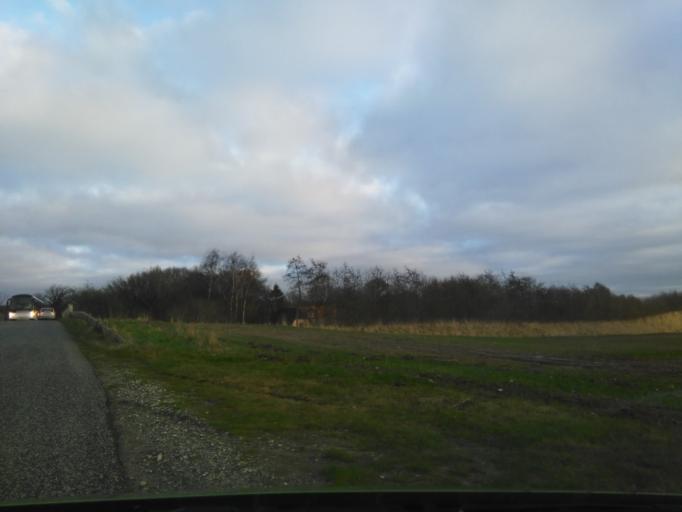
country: DK
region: Central Jutland
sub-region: Arhus Kommune
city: Framlev
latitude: 56.1676
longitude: 10.0596
